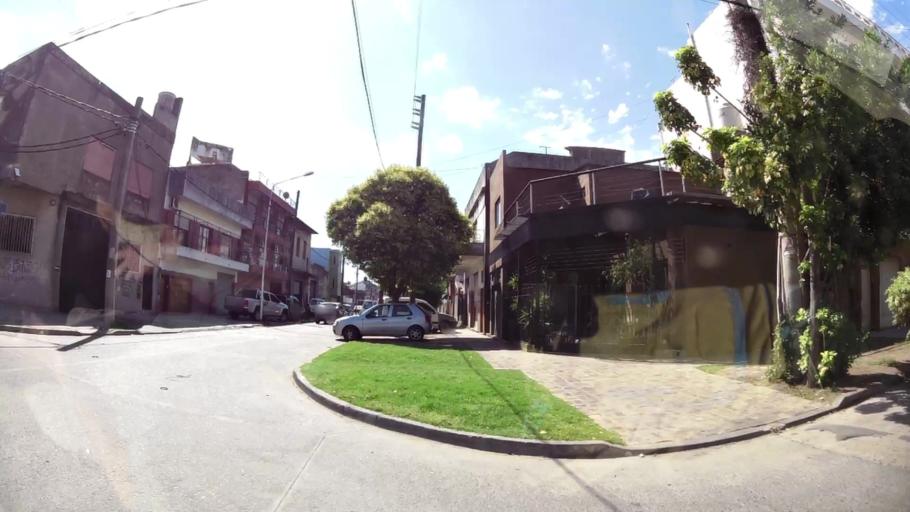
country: AR
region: Buenos Aires
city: San Justo
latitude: -34.6571
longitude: -58.5312
